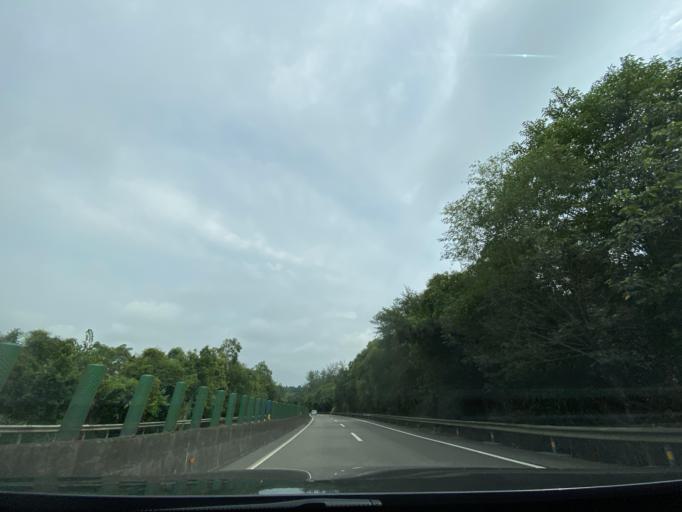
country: CN
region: Sichuan
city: Chonglong
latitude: 29.7257
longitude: 104.9220
